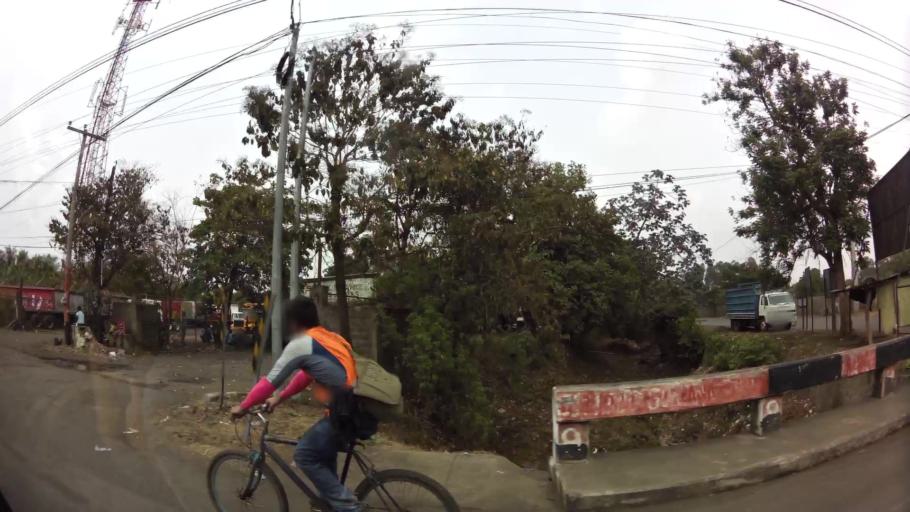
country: NI
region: Chinandega
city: Chinandega
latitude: 12.6351
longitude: -87.1193
